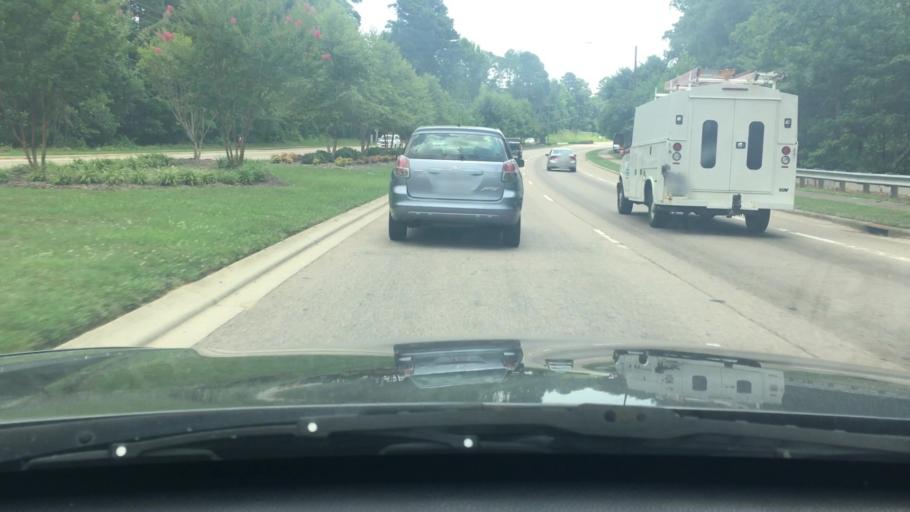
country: US
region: North Carolina
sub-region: Wake County
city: Cary
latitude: 35.7963
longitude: -78.7580
